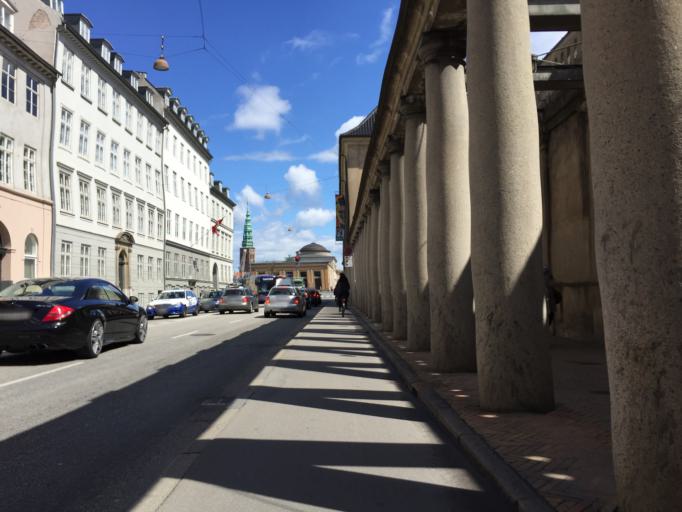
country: DK
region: Capital Region
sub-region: Kobenhavn
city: Copenhagen
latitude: 55.6751
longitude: 12.5746
